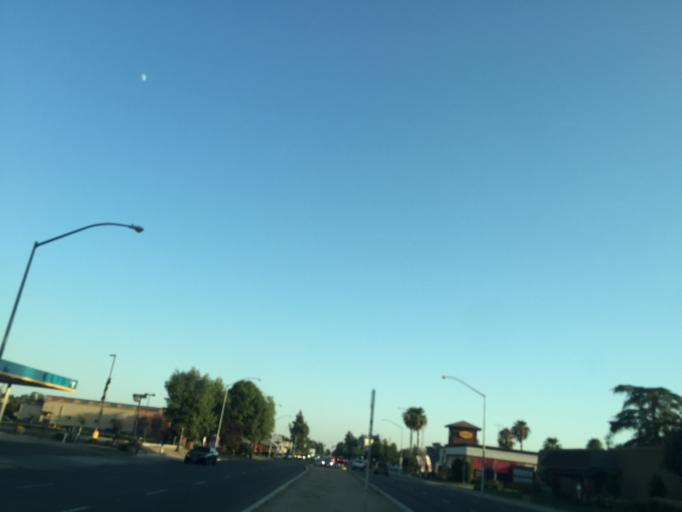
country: US
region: California
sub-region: Fresno County
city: Sunnyside
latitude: 36.7386
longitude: -119.7001
